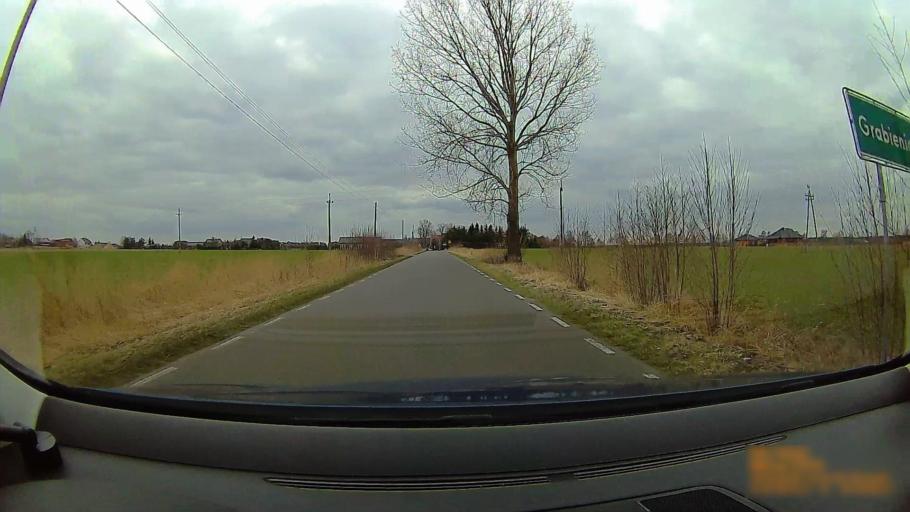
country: PL
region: Greater Poland Voivodeship
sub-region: Powiat koninski
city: Rzgow Pierwszy
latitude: 52.1374
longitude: 18.0568
